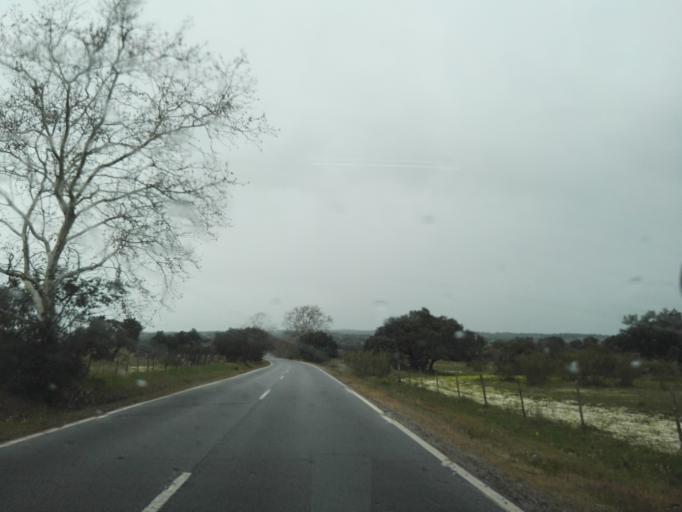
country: PT
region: Portalegre
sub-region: Arronches
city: Arronches
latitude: 39.0487
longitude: -7.2651
